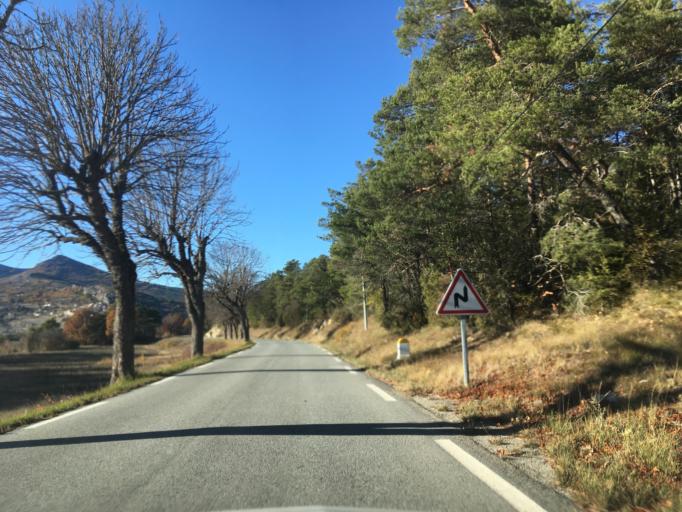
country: FR
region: Provence-Alpes-Cote d'Azur
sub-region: Departement des Alpes-de-Haute-Provence
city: Castellane
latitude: 43.7545
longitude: 6.4647
